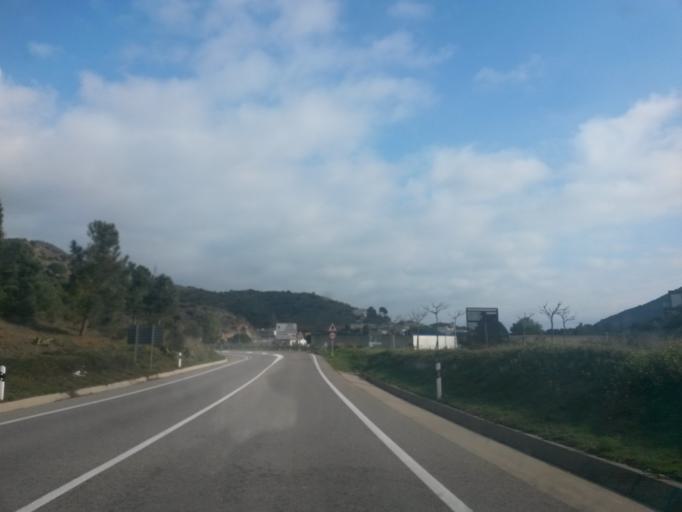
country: ES
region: Catalonia
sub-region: Provincia de Girona
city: Colera
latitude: 42.4018
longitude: 3.1438
